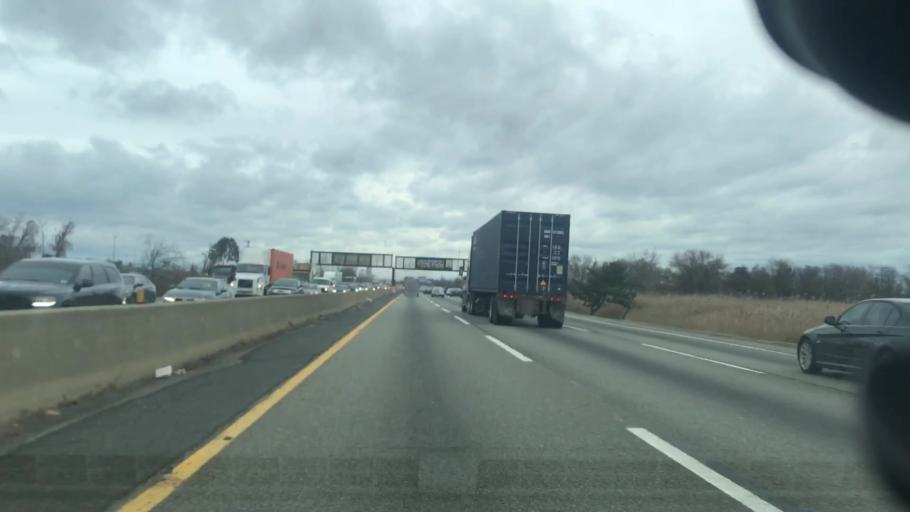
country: US
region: New Jersey
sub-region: Hudson County
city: North Bergen
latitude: 40.8168
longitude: -74.0282
